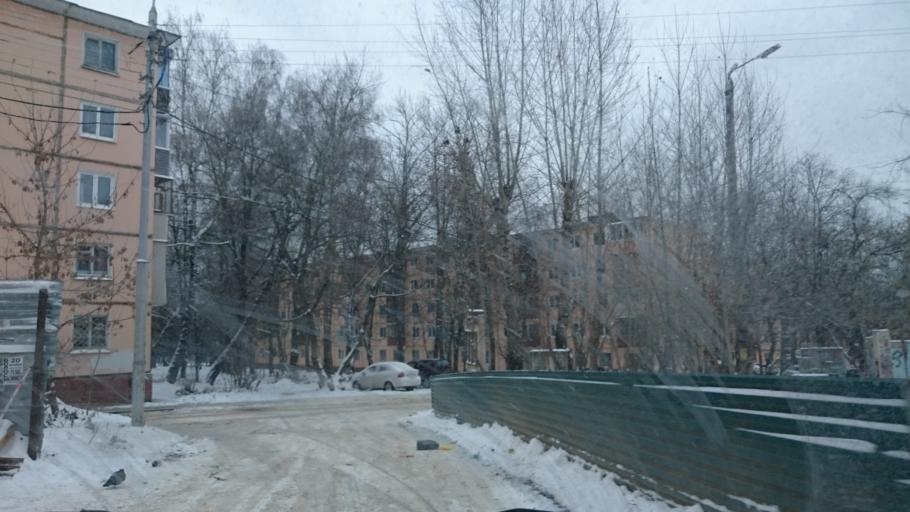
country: RU
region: Tula
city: Mendeleyevskiy
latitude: 54.1547
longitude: 37.5904
